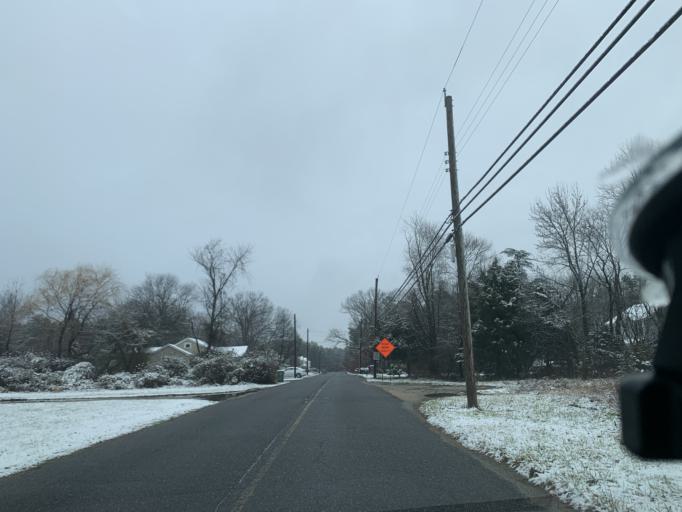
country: US
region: New Jersey
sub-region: Atlantic County
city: Pomona
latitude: 39.4325
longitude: -74.5961
